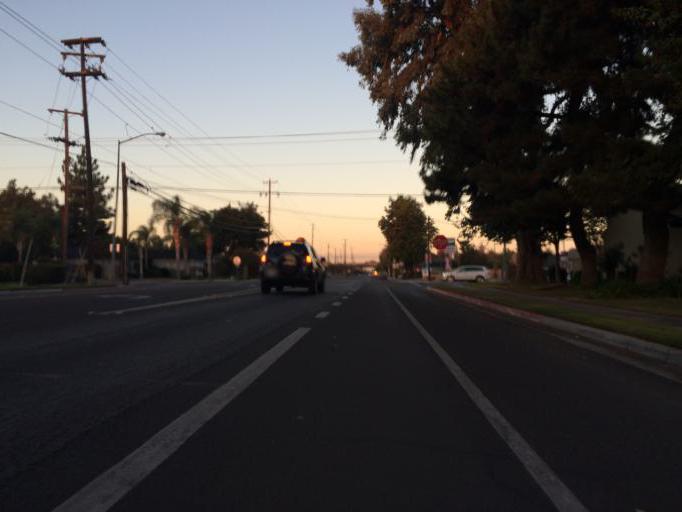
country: US
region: California
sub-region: Fresno County
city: Tarpey Village
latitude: 36.8013
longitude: -119.7357
